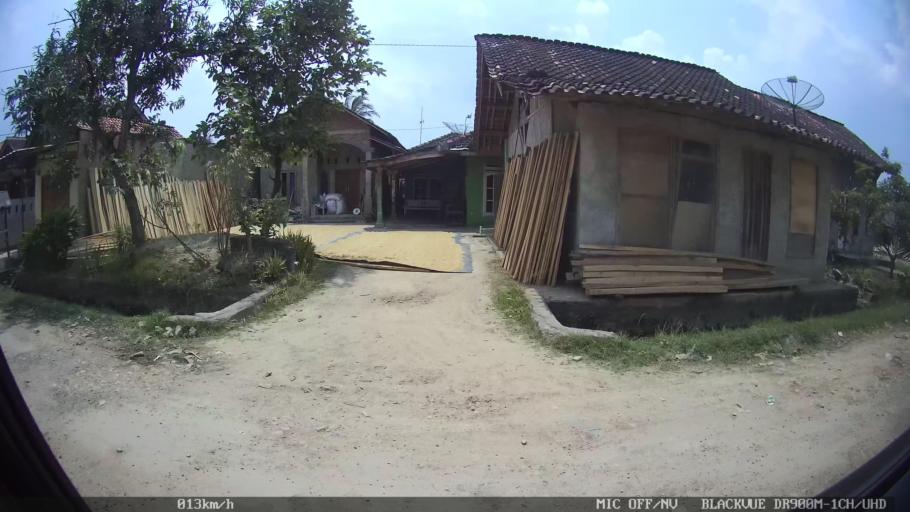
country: ID
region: Lampung
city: Pringsewu
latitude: -5.3664
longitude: 105.0000
